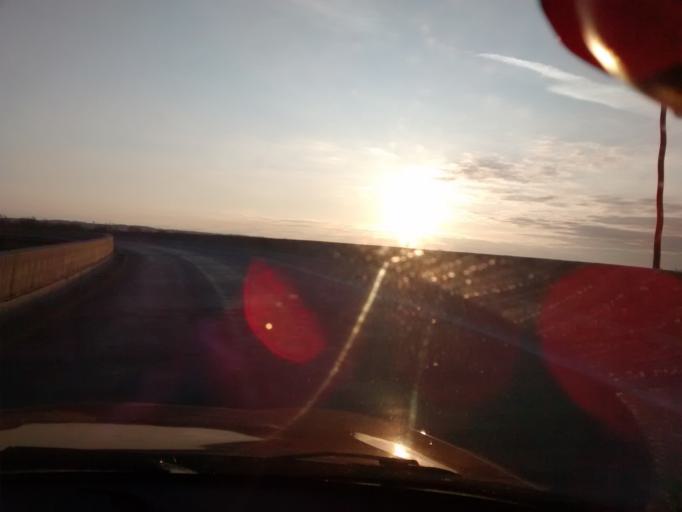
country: US
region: Nebraska
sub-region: Douglas County
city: Omaha
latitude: 41.2616
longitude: -95.9096
